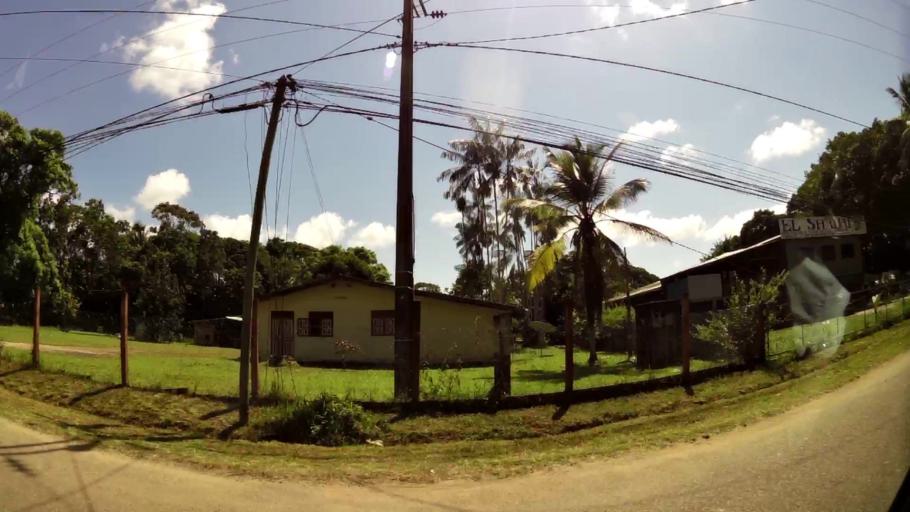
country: GF
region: Guyane
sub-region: Guyane
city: Matoury
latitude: 4.8338
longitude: -52.3238
